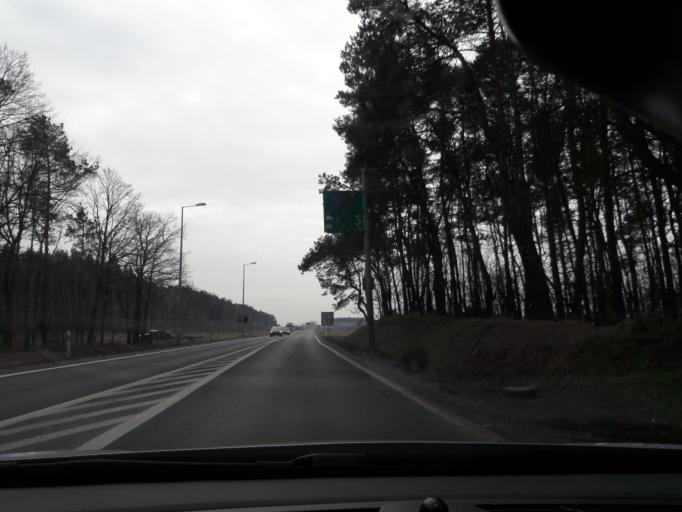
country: PL
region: Greater Poland Voivodeship
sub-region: Powiat poznanski
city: Zlotniki
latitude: 52.5295
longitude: 16.8338
